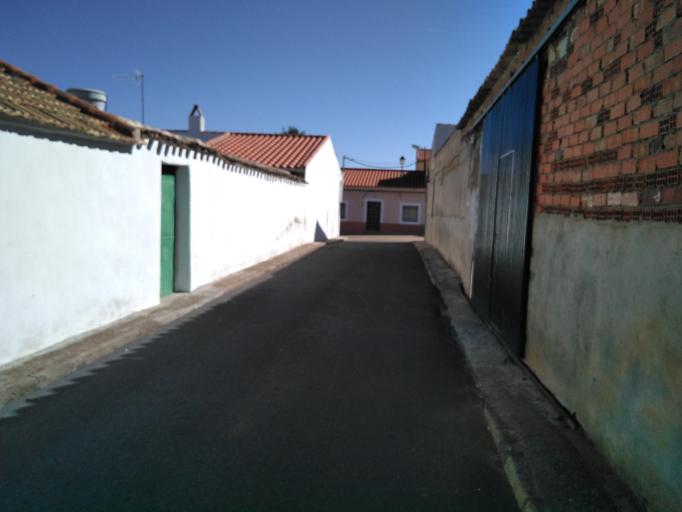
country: ES
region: Castille-La Mancha
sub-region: Provincia de Ciudad Real
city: Ballesteros de Calatrava
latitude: 38.8330
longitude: -3.9467
